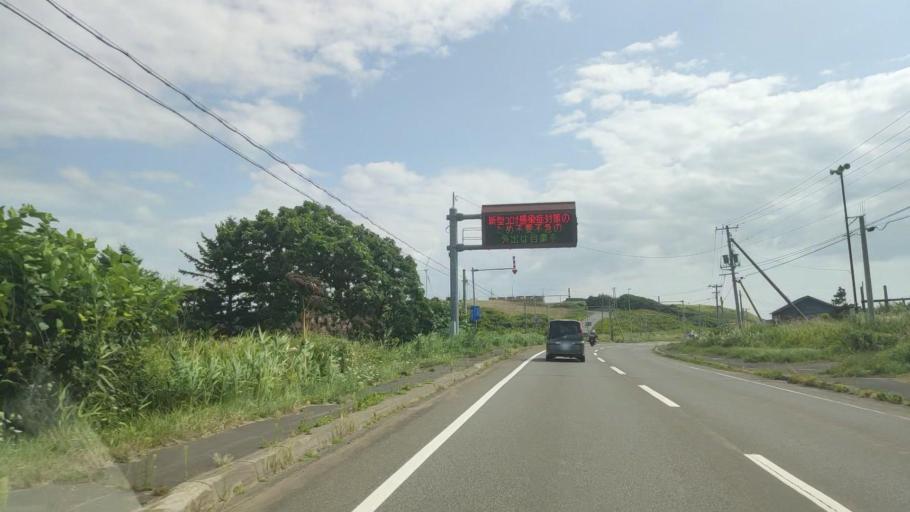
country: JP
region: Hokkaido
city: Rumoi
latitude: 44.2595
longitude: 141.6570
